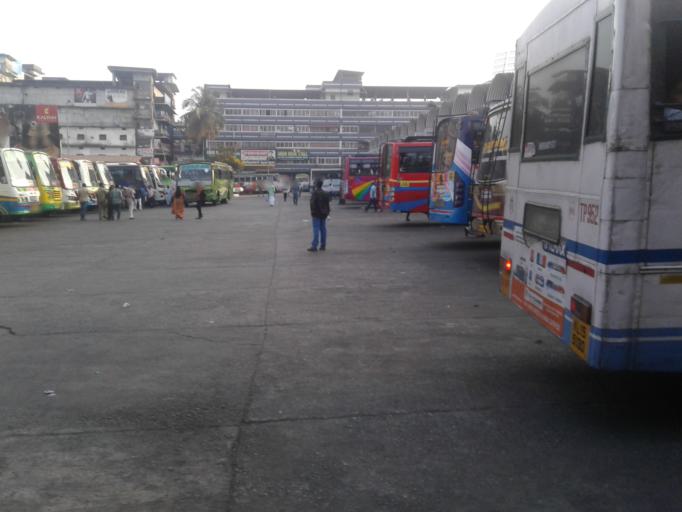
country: IN
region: Kerala
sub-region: Kozhikode
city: Kozhikode
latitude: 11.2589
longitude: 75.7872
